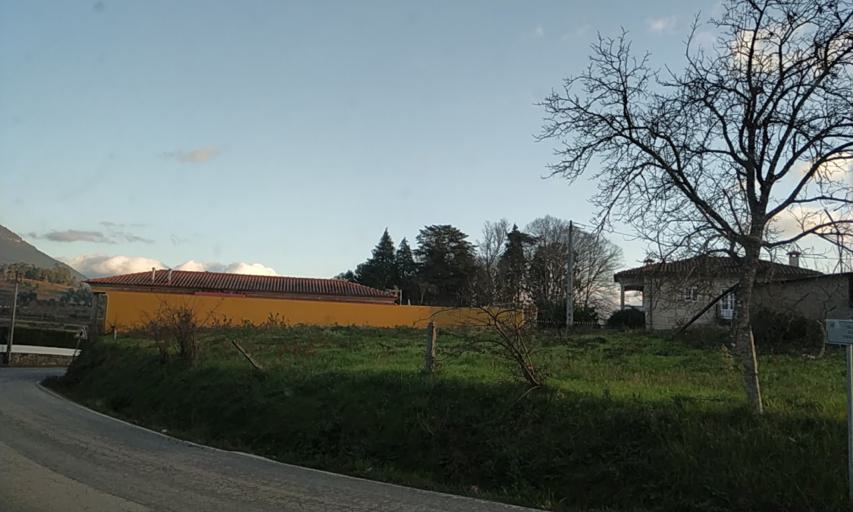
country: PT
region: Vila Real
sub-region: Mondim de Basto
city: Mondim de Basto
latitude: 41.4250
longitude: -7.9860
